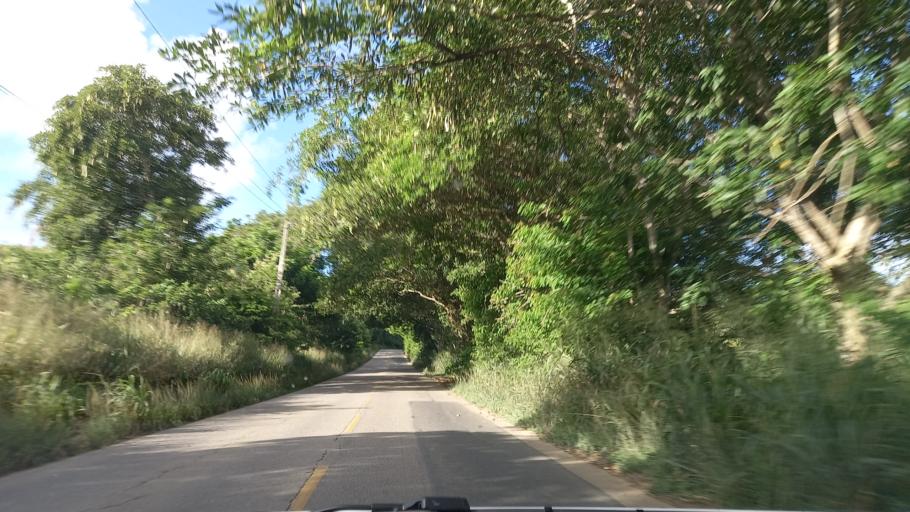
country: BR
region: Pernambuco
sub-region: Rio Formoso
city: Rio Formoso
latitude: -8.6541
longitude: -35.1356
